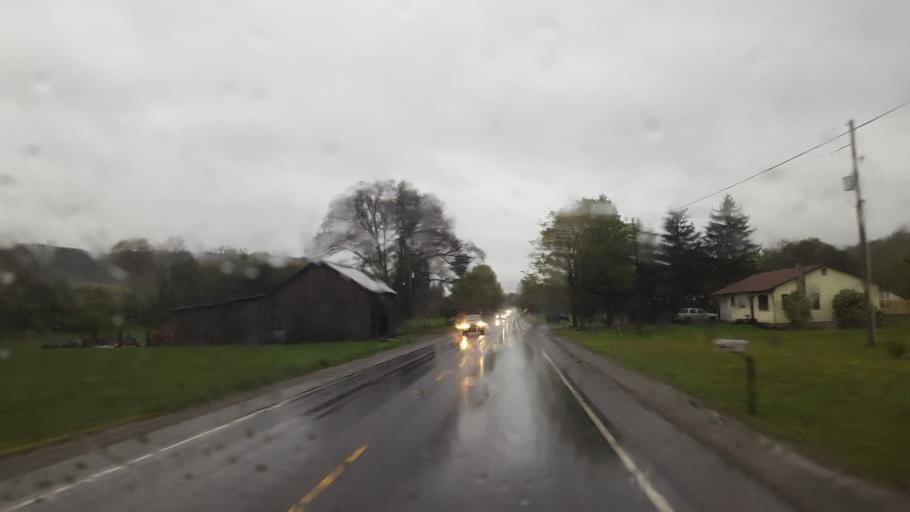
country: US
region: Pennsylvania
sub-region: Tioga County
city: Westfield
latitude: 41.9295
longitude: -77.5077
